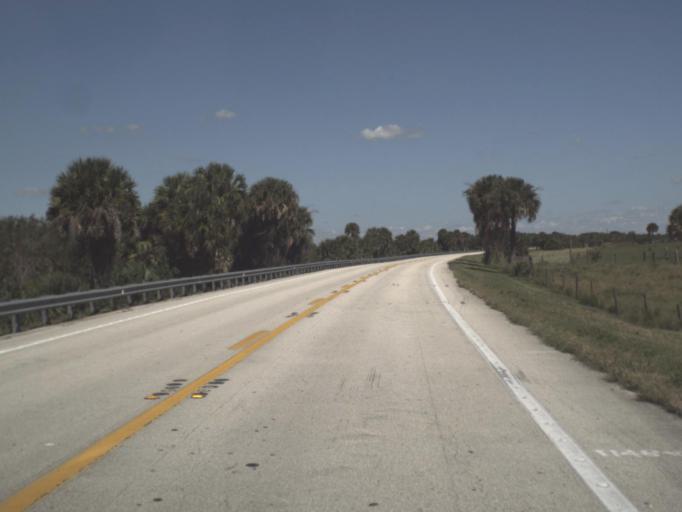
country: US
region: Florida
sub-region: Glades County
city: Buckhead Ridge
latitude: 27.0770
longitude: -80.9735
